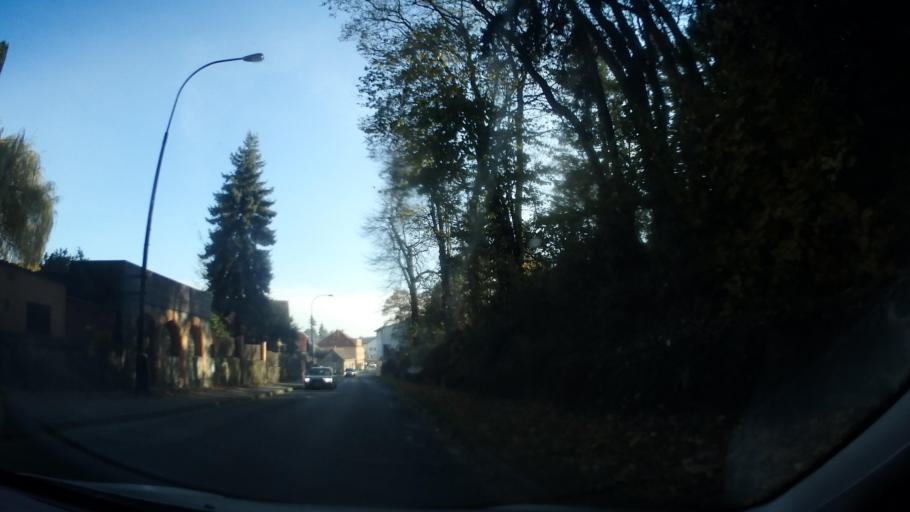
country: CZ
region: Central Bohemia
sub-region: Okres Praha-Vychod
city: Mnichovice
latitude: 49.9376
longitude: 14.7062
